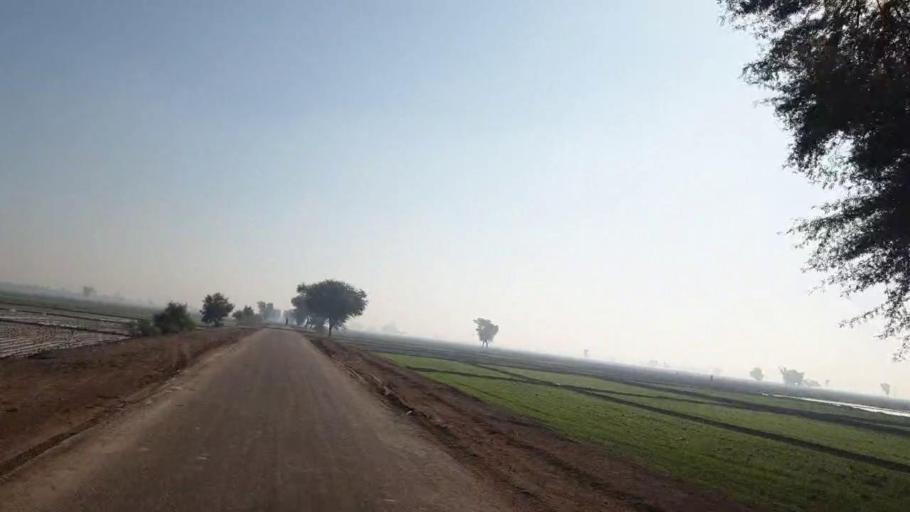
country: PK
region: Sindh
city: Dadu
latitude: 26.6723
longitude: 67.8273
